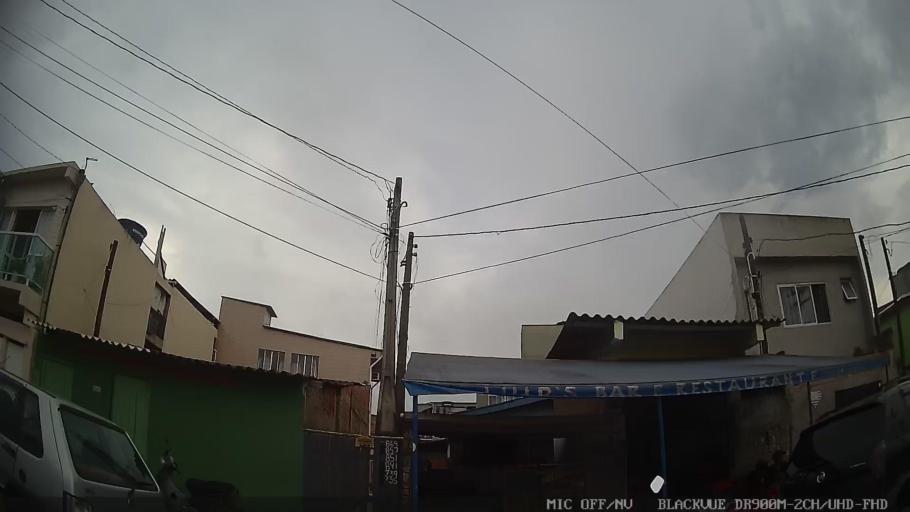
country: BR
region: Sao Paulo
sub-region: Guaruja
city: Guaruja
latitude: -23.9775
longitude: -46.2268
